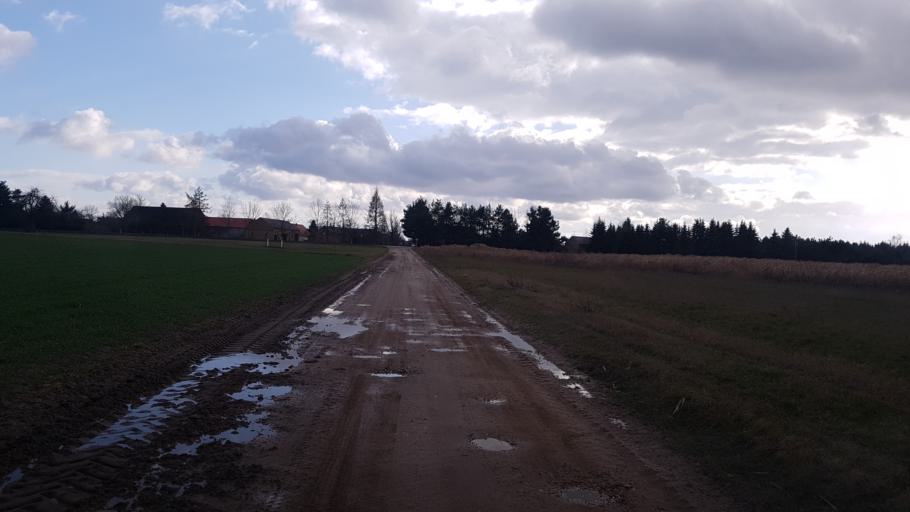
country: DE
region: Brandenburg
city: Sallgast
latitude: 51.6130
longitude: 13.8556
